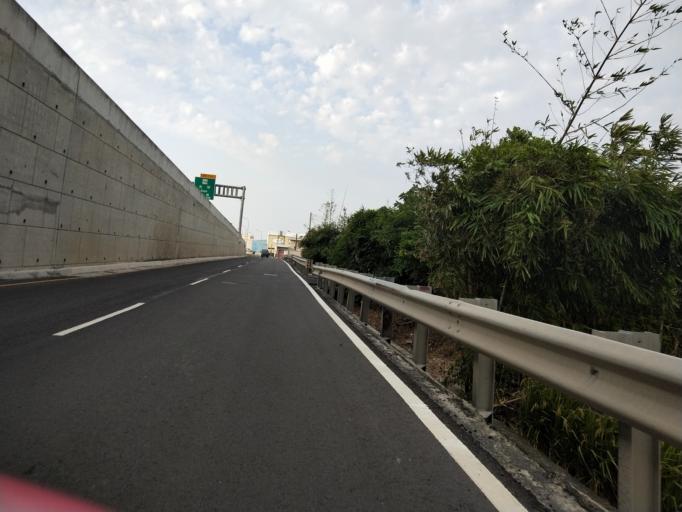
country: TW
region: Taiwan
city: Fengyuan
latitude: 24.3623
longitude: 120.5857
